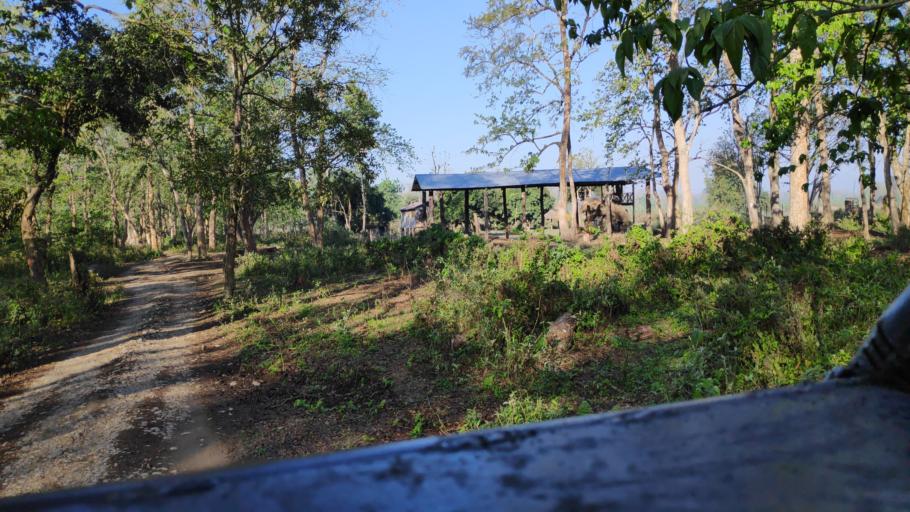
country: NP
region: Central Region
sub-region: Narayani Zone
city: Bharatpur
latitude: 27.5590
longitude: 84.5591
